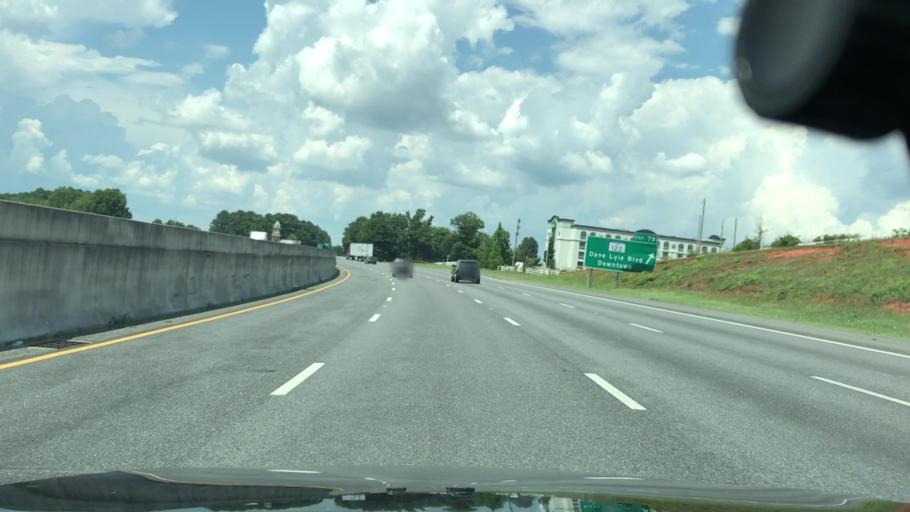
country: US
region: South Carolina
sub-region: York County
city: Lesslie
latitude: 34.9353
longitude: -80.9712
